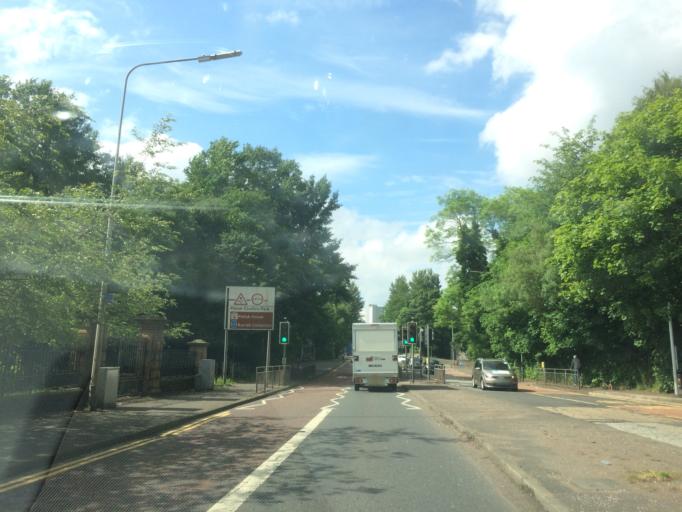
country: GB
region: Scotland
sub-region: East Renfrewshire
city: Giffnock
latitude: 55.8257
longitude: -4.2989
